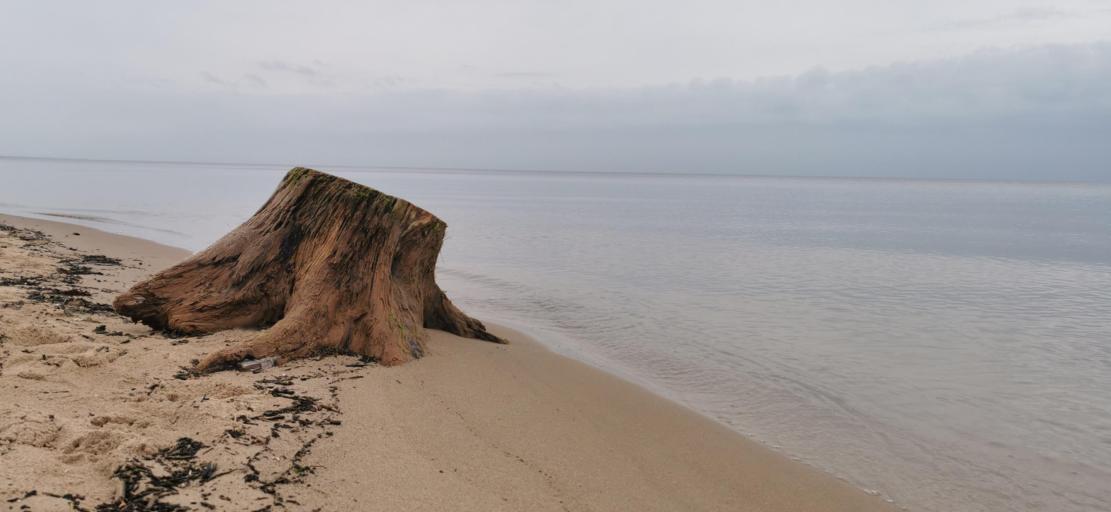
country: LV
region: Carnikava
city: Carnikava
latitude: 57.1467
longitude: 24.2451
